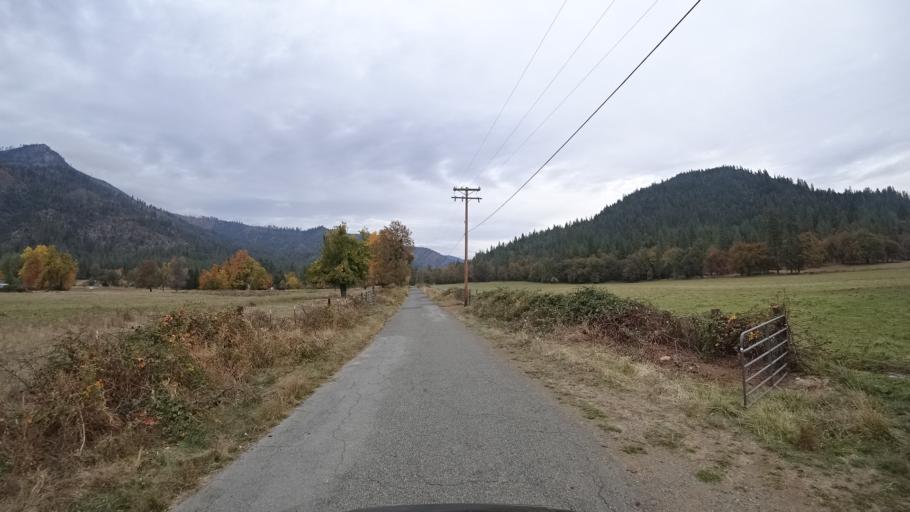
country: US
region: California
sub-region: Siskiyou County
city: Happy Camp
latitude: 41.8406
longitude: -123.1914
